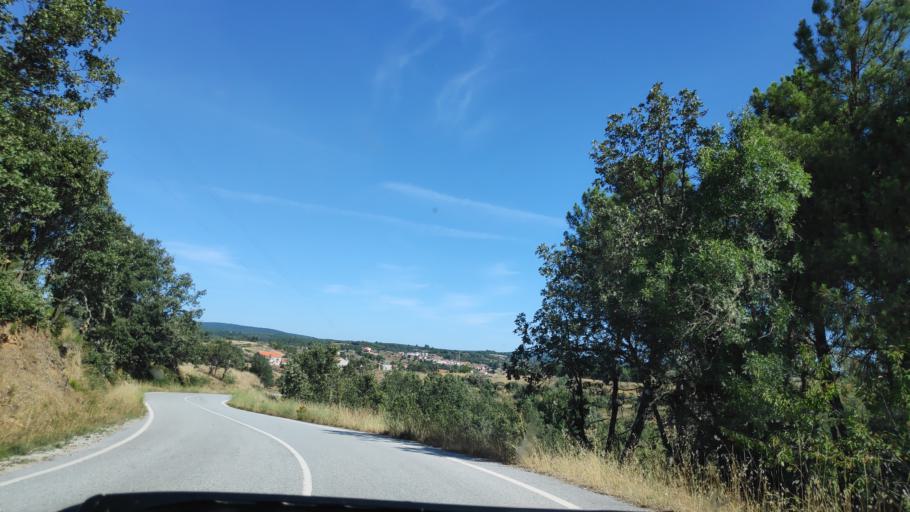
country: ES
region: Castille and Leon
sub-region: Provincia de Zamora
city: Alcanices
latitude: 41.6283
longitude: -6.3488
